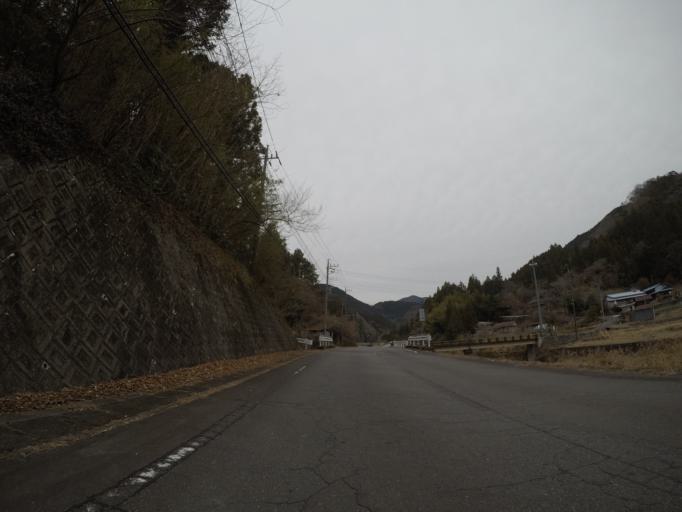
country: JP
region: Shizuoka
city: Fujinomiya
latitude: 35.2658
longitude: 138.5305
